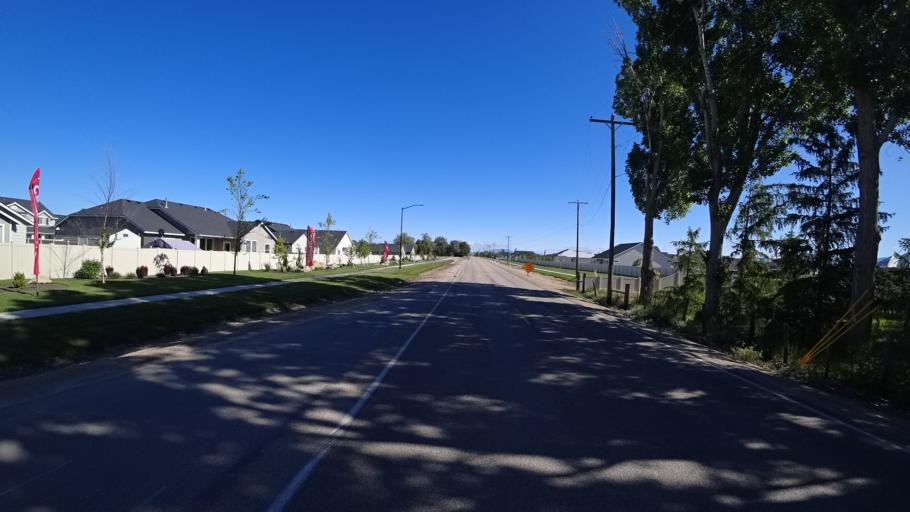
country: US
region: Idaho
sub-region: Ada County
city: Star
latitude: 43.6532
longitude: -116.4537
